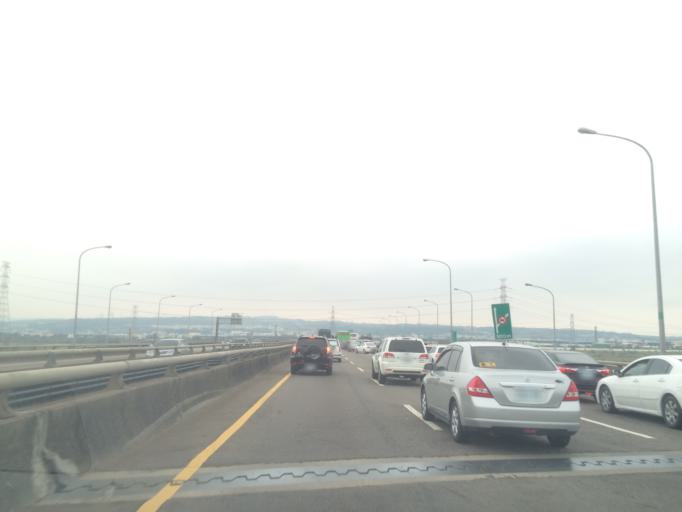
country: TW
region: Taiwan
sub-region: Changhua
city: Chang-hua
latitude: 24.1019
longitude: 120.6123
